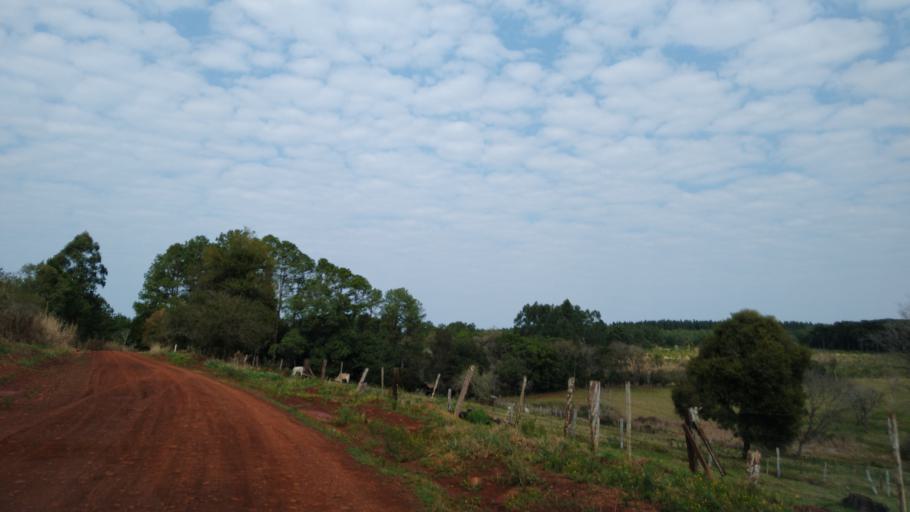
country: AR
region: Misiones
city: Capiovi
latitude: -26.9430
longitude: -55.0683
